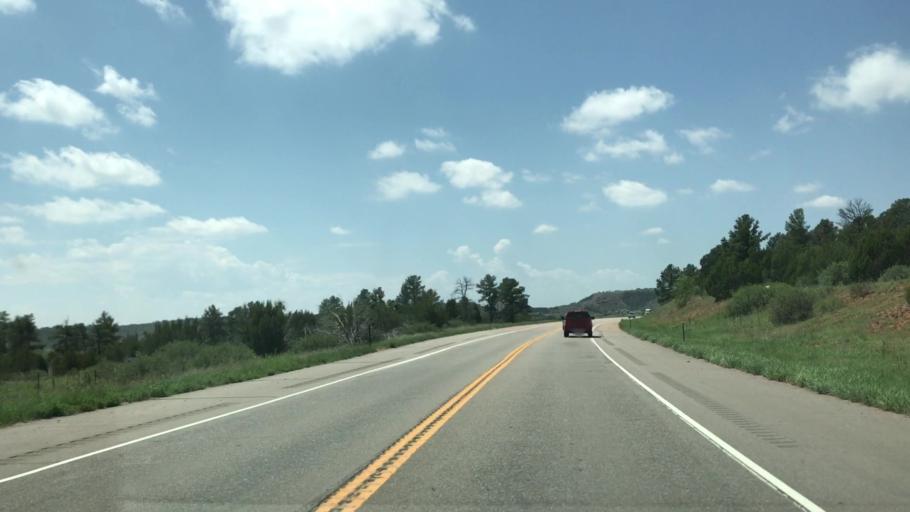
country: US
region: Colorado
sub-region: El Paso County
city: Fort Carson
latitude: 38.6243
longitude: -104.8763
